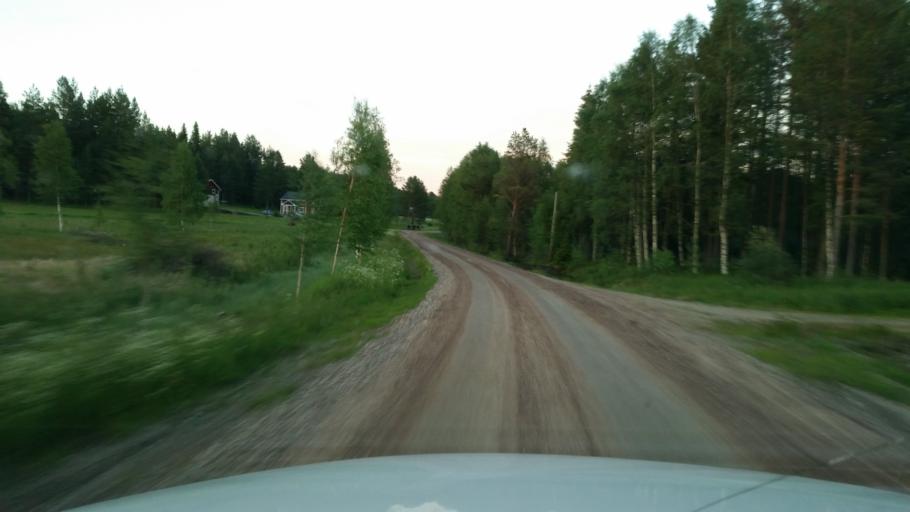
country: SE
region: Vaesternorrland
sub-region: Ange Kommun
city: Ange
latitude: 62.1850
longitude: 15.6321
